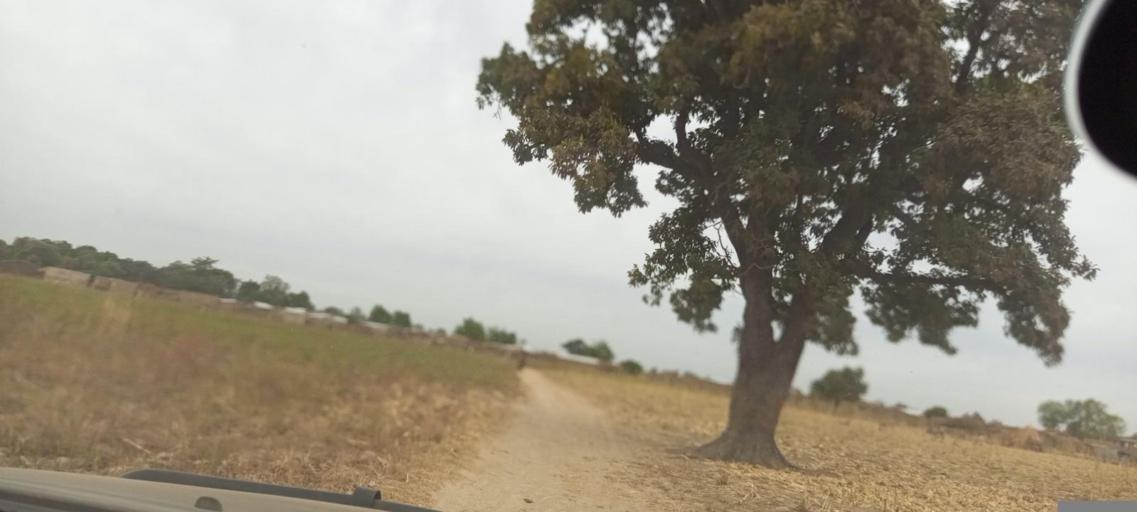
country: ML
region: Koulikoro
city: Kati
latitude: 12.7473
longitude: -8.3583
